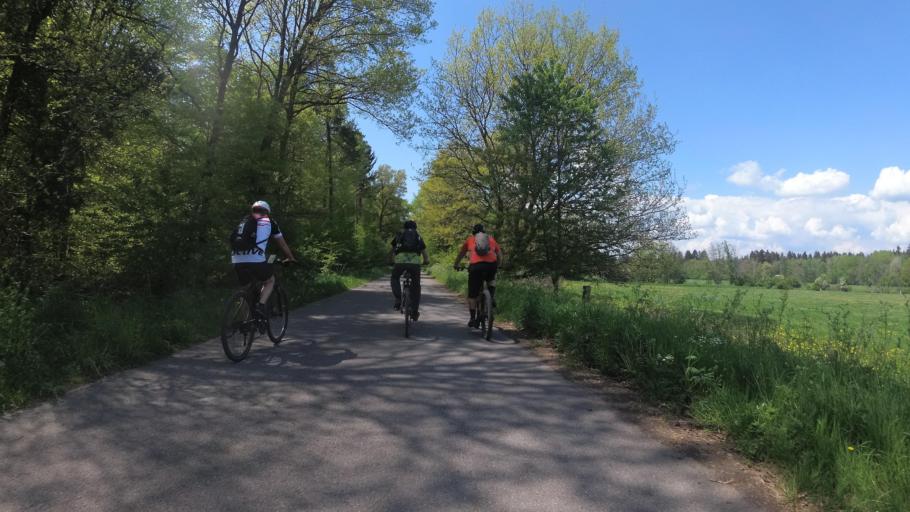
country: DE
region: Rheinland-Pfalz
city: Schonenberg-Kubelberg
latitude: 49.3816
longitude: 7.3658
